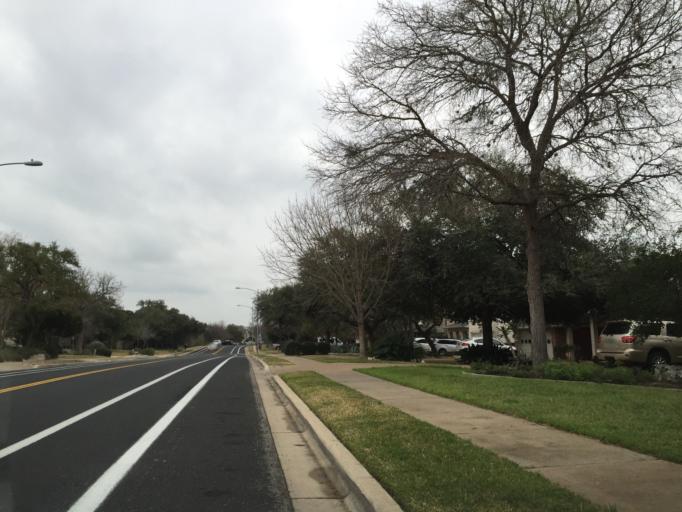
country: US
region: Texas
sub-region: Travis County
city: Barton Creek
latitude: 30.2502
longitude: -97.8418
